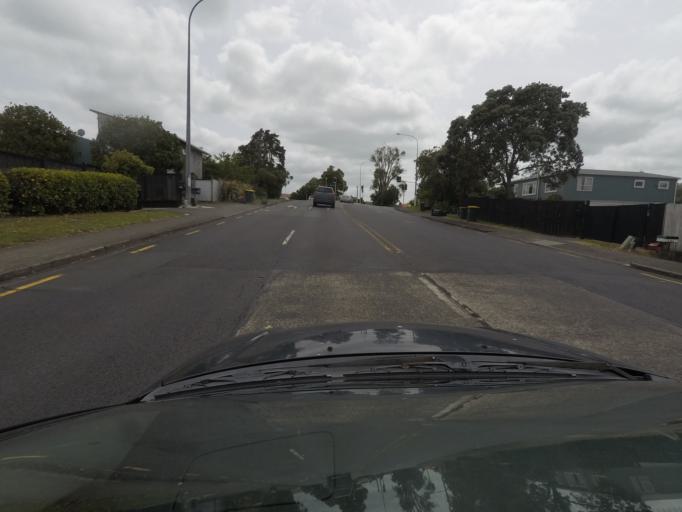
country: NZ
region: Auckland
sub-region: Auckland
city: Pakuranga
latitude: -36.8935
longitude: 174.9239
